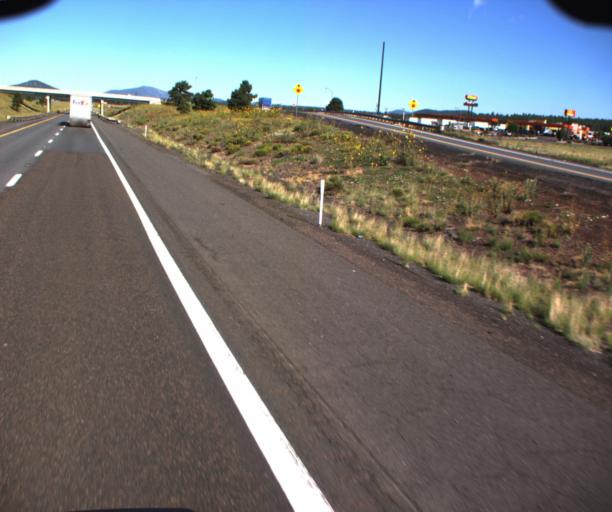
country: US
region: Arizona
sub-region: Coconino County
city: Parks
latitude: 35.2357
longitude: -111.8208
